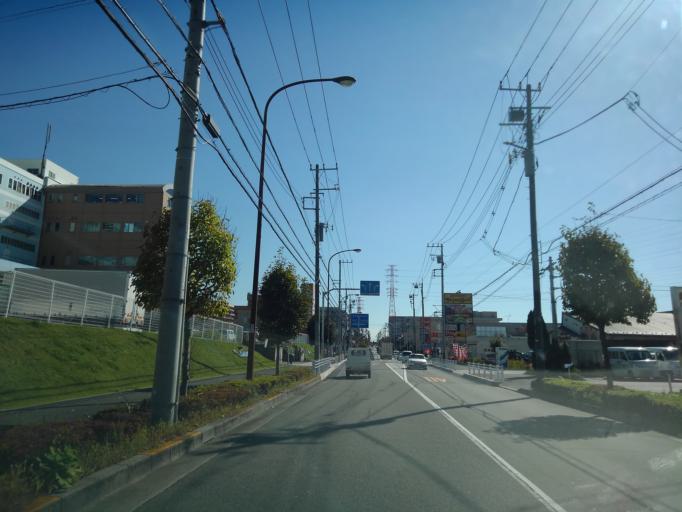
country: JP
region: Tokyo
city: Hino
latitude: 35.6000
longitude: 139.3802
